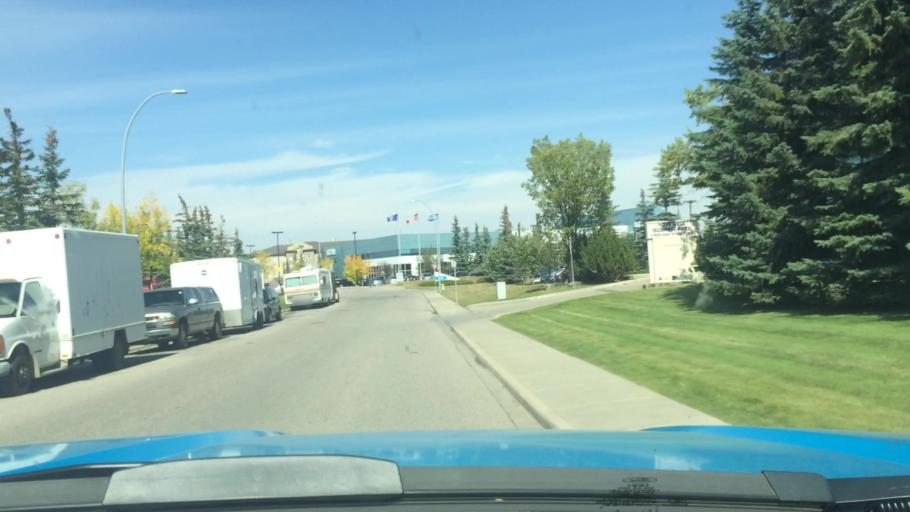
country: CA
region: Alberta
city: Calgary
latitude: 51.0904
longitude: -113.9977
